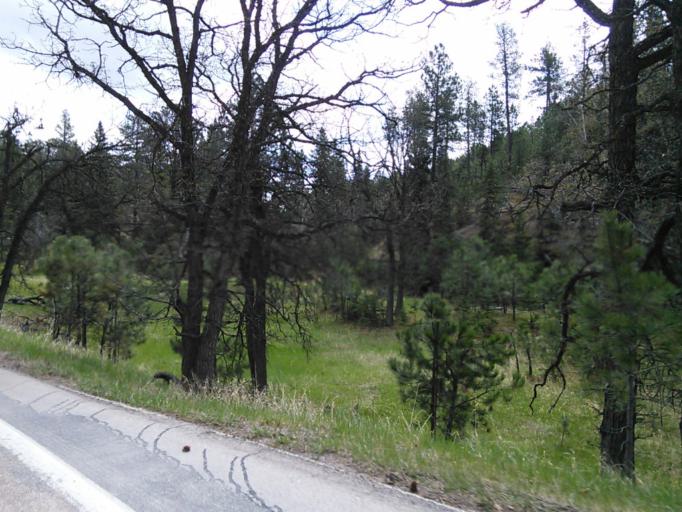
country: US
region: South Dakota
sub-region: Custer County
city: Custer
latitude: 43.7622
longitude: -103.4715
